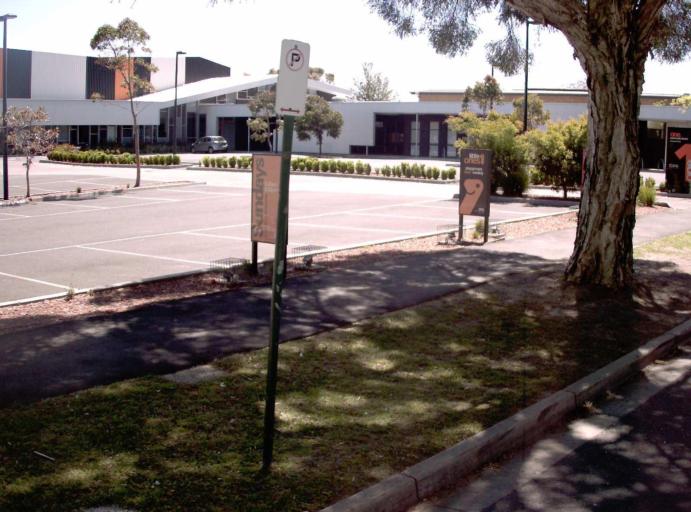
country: AU
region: Victoria
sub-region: Whitehorse
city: Blackburn
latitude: -37.8161
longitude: 145.1566
